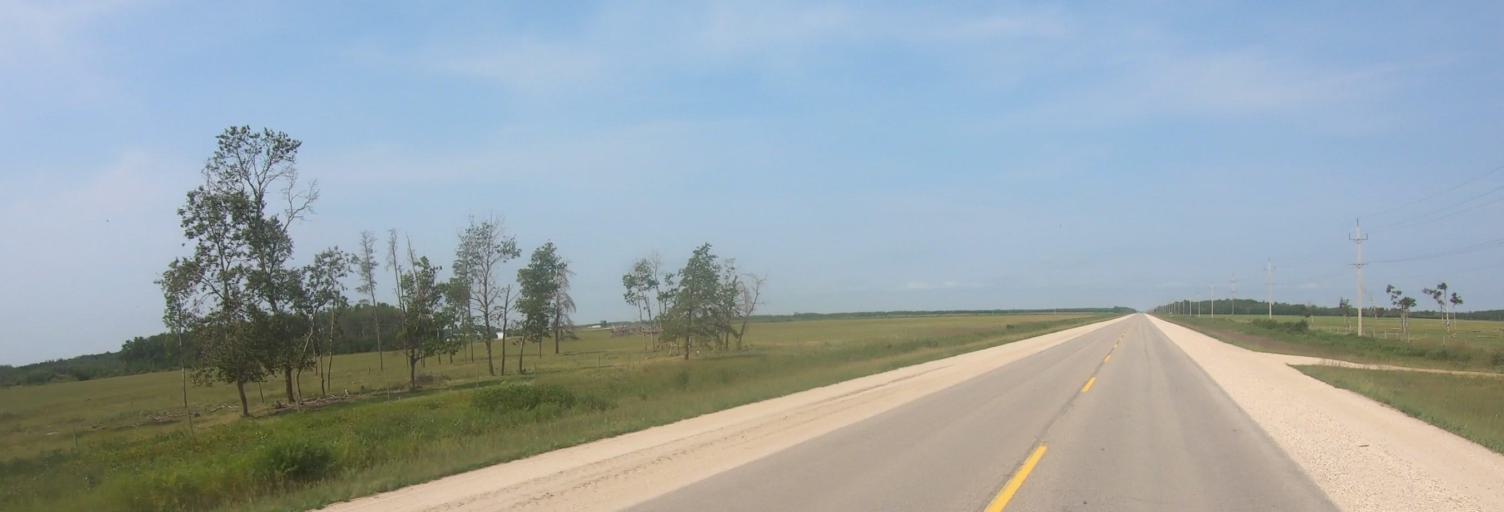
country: CA
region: Manitoba
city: La Broquerie
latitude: 49.3117
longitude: -96.5689
